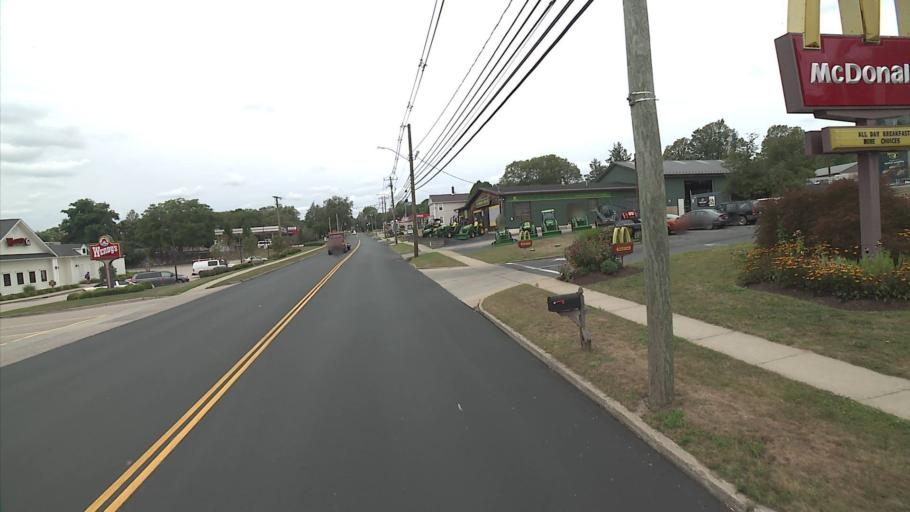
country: US
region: Connecticut
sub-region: New London County
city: Colchester
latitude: 41.5676
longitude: -72.3258
